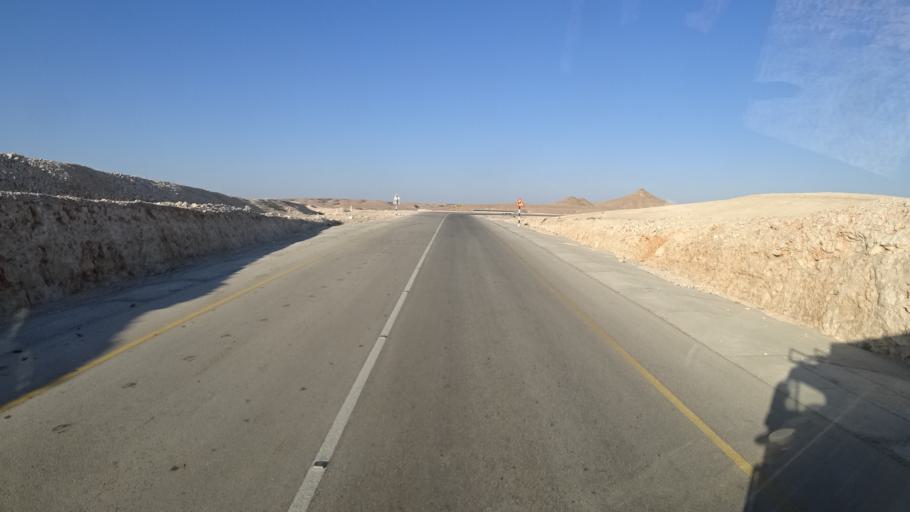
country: YE
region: Al Mahrah
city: Hawf
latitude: 17.0939
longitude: 53.0640
